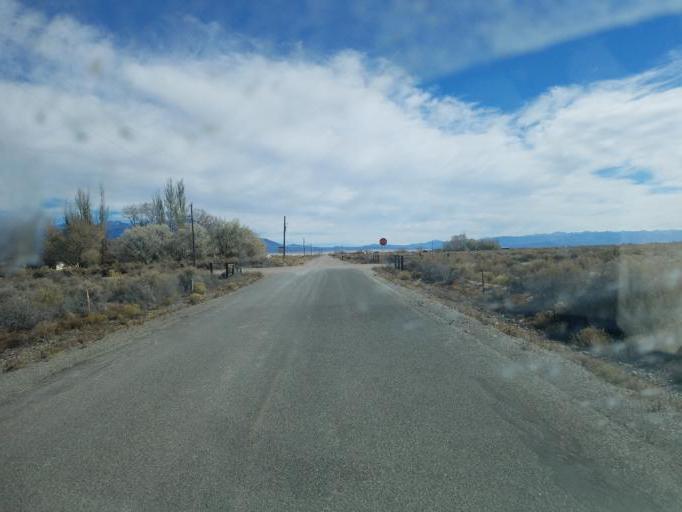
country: US
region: Colorado
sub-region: Alamosa County
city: Alamosa East
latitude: 37.5028
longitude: -105.7855
